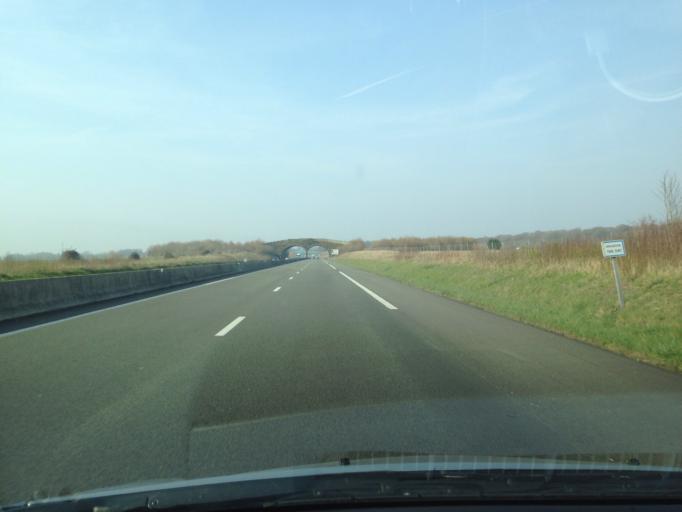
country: FR
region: Picardie
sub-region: Departement de la Somme
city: Nouvion
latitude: 50.2282
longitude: 1.7522
